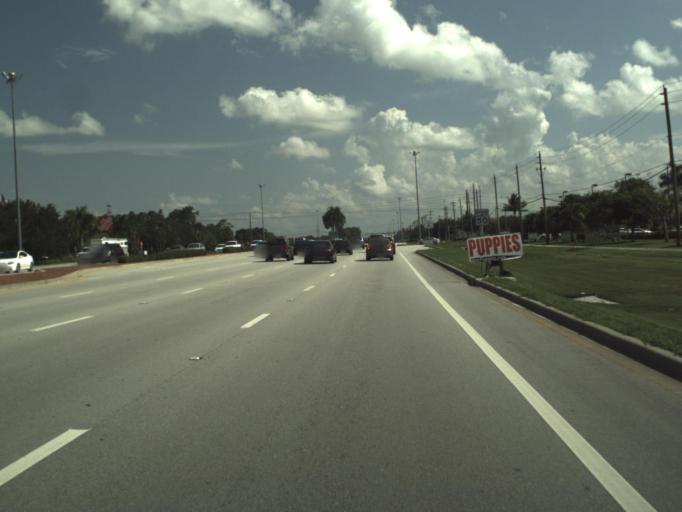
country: US
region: Florida
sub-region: Palm Beach County
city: Royal Palm Beach
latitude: 26.6782
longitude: -80.2026
